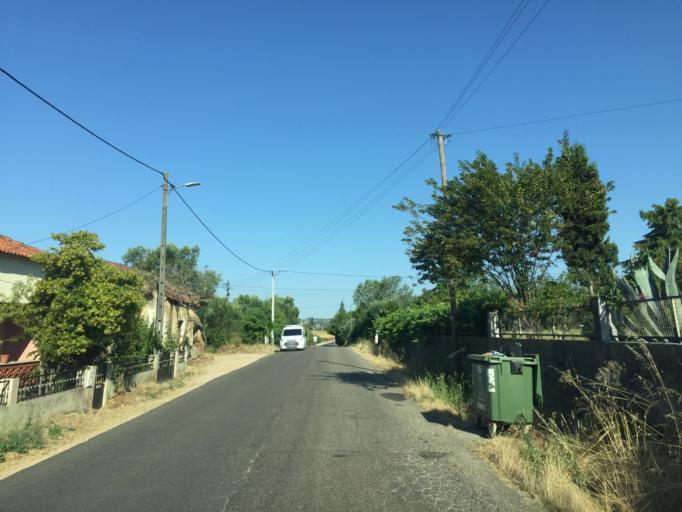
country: PT
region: Santarem
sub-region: Tomar
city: Tomar
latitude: 39.5973
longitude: -8.3791
